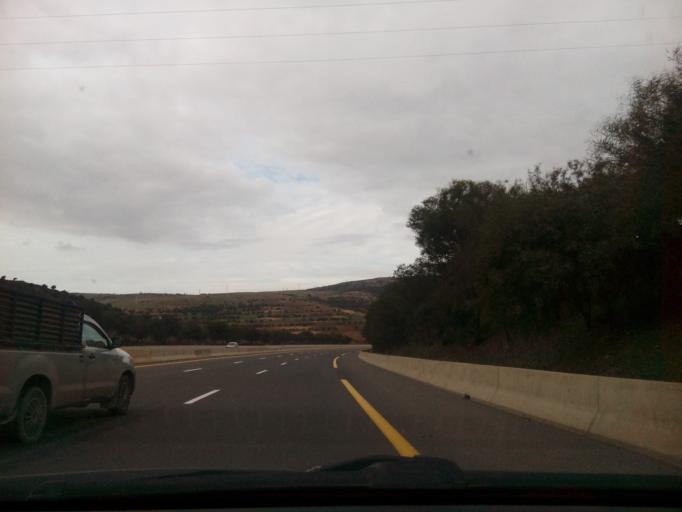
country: DZ
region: Sidi Bel Abbes
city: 'Ain el Berd
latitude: 35.4003
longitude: -0.4914
